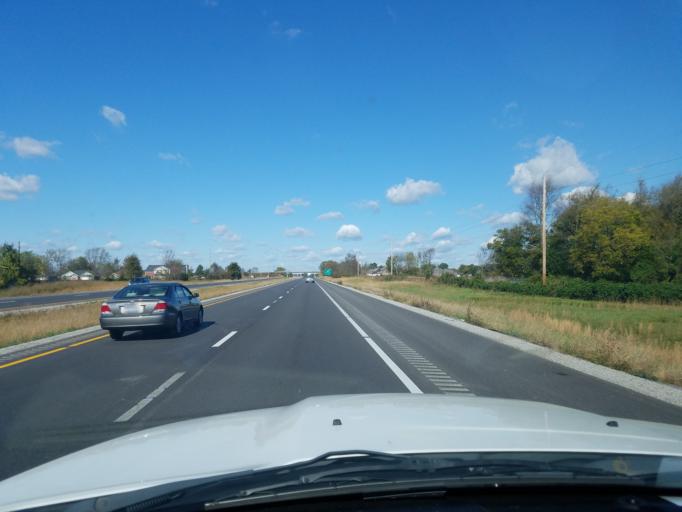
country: US
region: Kentucky
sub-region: Warren County
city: Plano
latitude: 36.9216
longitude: -86.4479
